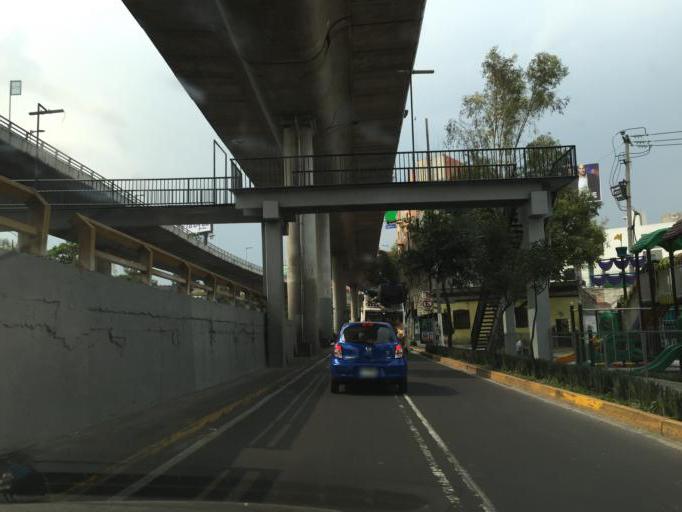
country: MX
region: Mexico City
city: Alvaro Obregon
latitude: 19.3675
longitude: -99.1912
